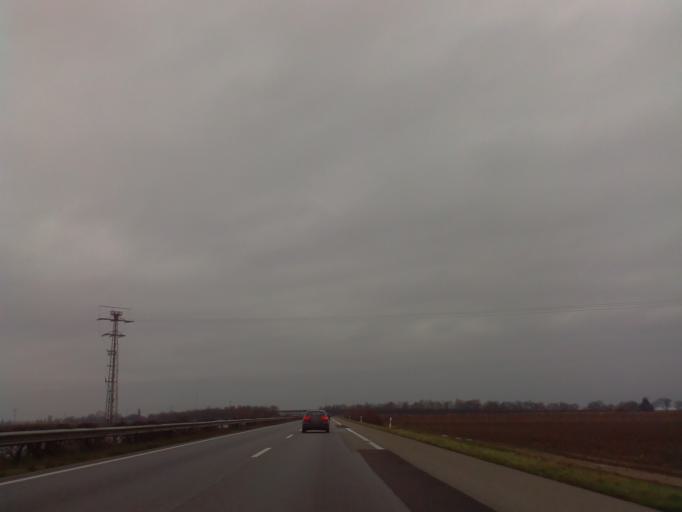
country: DE
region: Rheinland-Pfalz
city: Hochdorf-Assenheim
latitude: 49.4153
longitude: 8.2872
